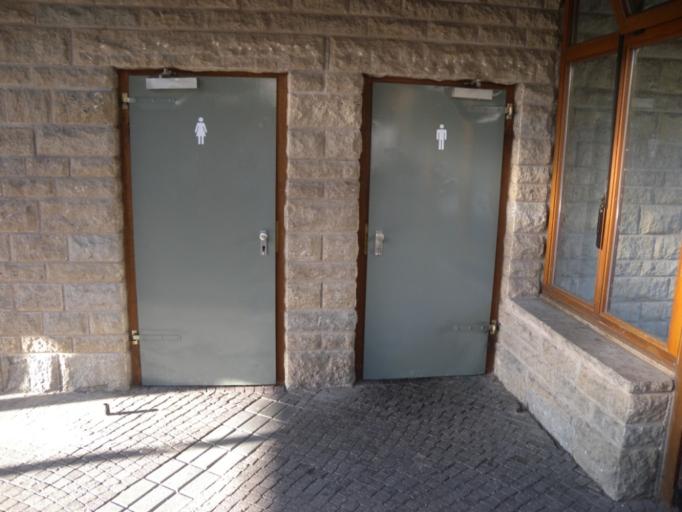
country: DE
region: Baden-Wuerttemberg
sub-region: Regierungsbezirk Stuttgart
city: Crailsheim
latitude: 49.1374
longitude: 10.0675
